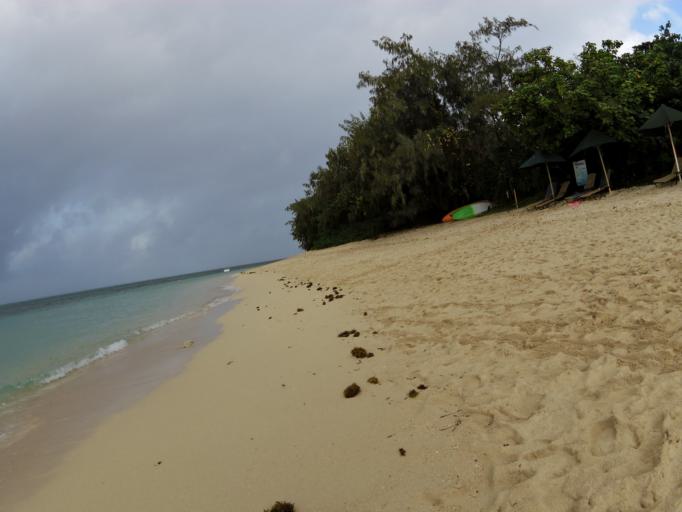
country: AU
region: Queensland
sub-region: Cairns
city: Yorkeys Knob
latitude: -16.7578
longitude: 145.9731
